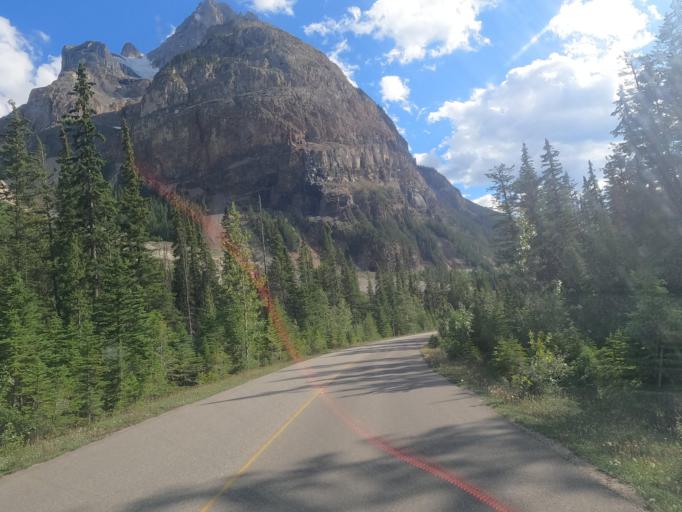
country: CA
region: Alberta
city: Lake Louise
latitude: 51.4221
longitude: -116.4381
